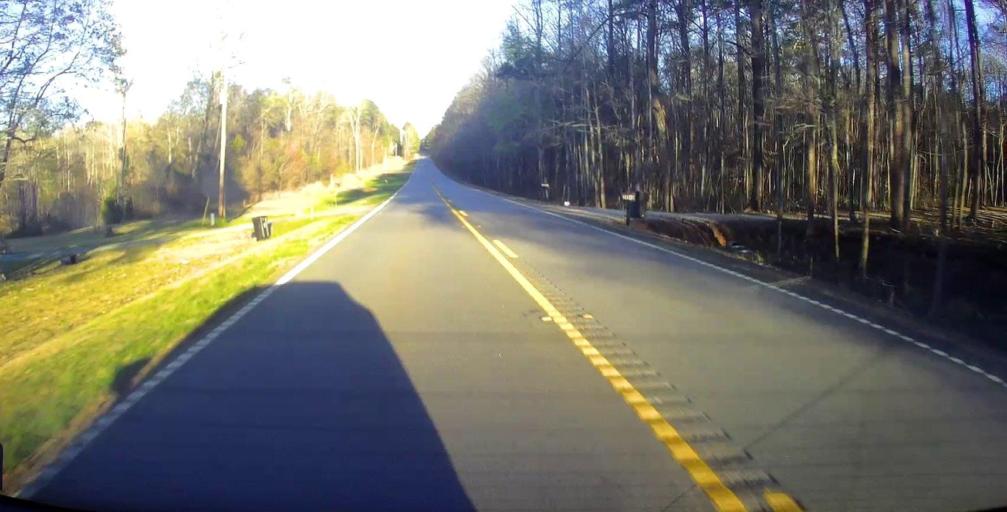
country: US
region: Georgia
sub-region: Harris County
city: Hamilton
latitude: 32.6322
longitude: -84.7426
